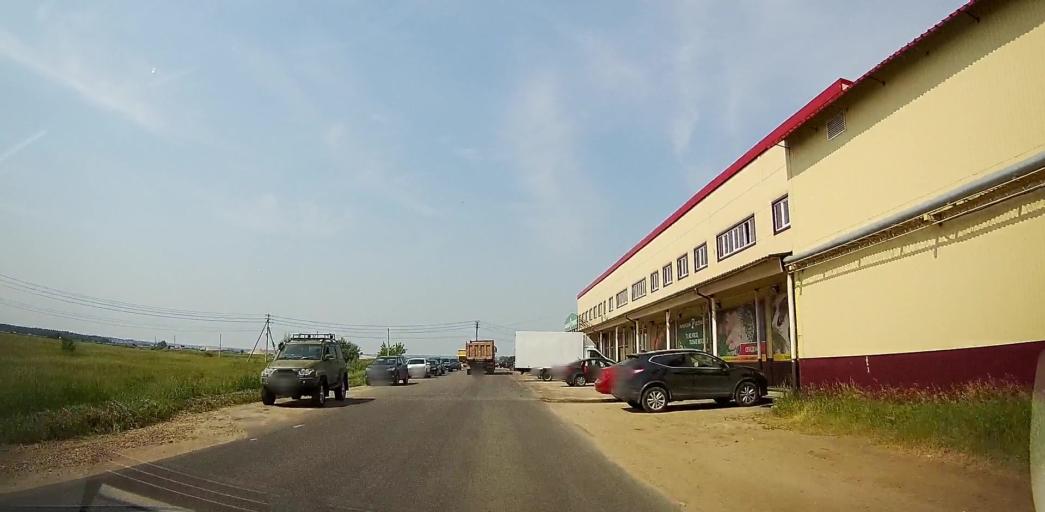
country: RU
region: Moskovskaya
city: Malyshevo
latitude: 55.5078
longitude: 38.2986
